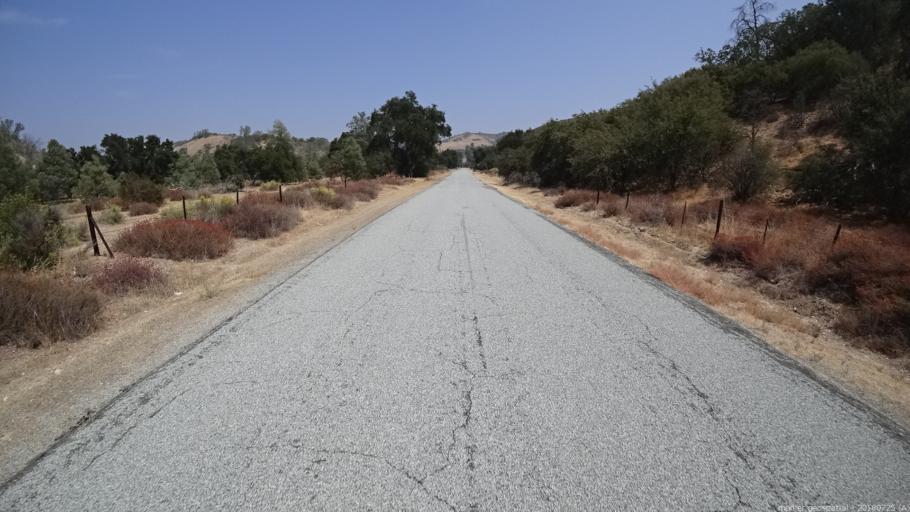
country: US
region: California
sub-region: San Luis Obispo County
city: San Miguel
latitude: 35.8605
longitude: -120.5829
